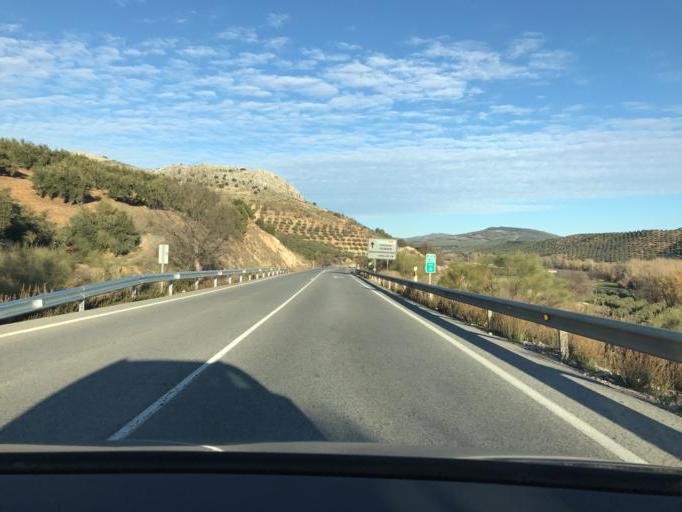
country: ES
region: Andalusia
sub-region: Provincia de Granada
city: Iznalloz
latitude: 37.4017
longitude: -3.5233
